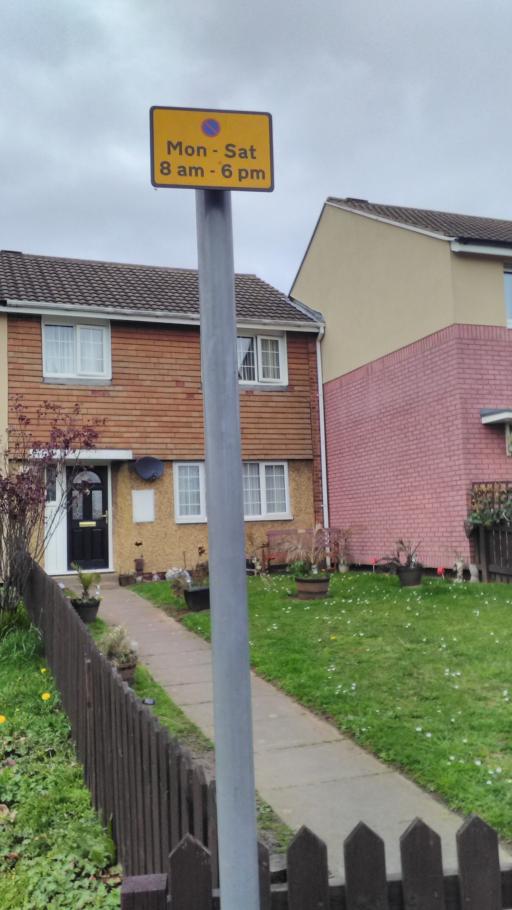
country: GB
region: England
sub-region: Nottingham
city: Nottingham
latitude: 52.9572
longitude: -1.1356
